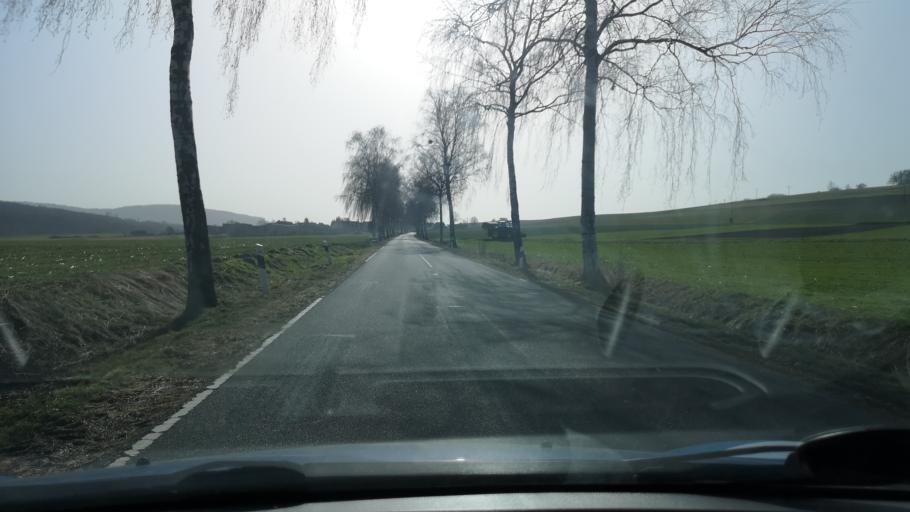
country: DE
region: Lower Saxony
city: Weenzen
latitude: 51.9985
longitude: 9.6463
